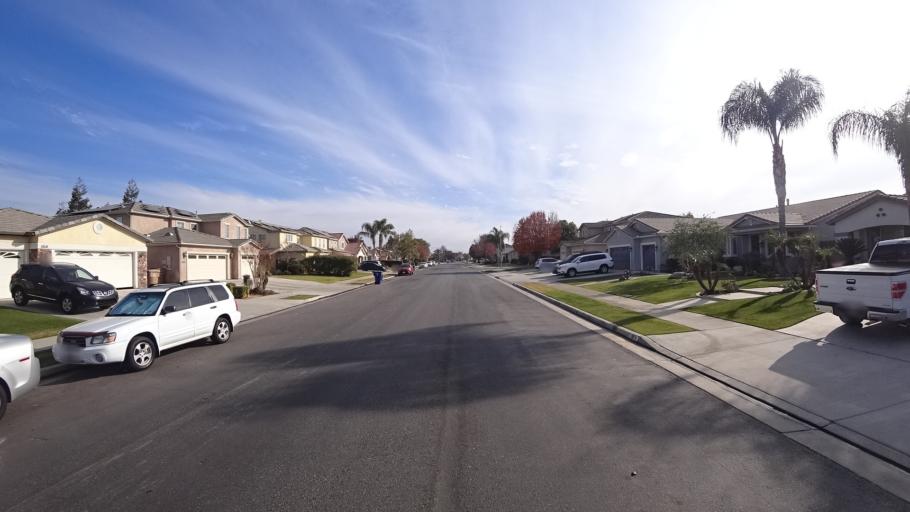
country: US
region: California
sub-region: Kern County
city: Rosedale
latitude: 35.4066
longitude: -119.1320
